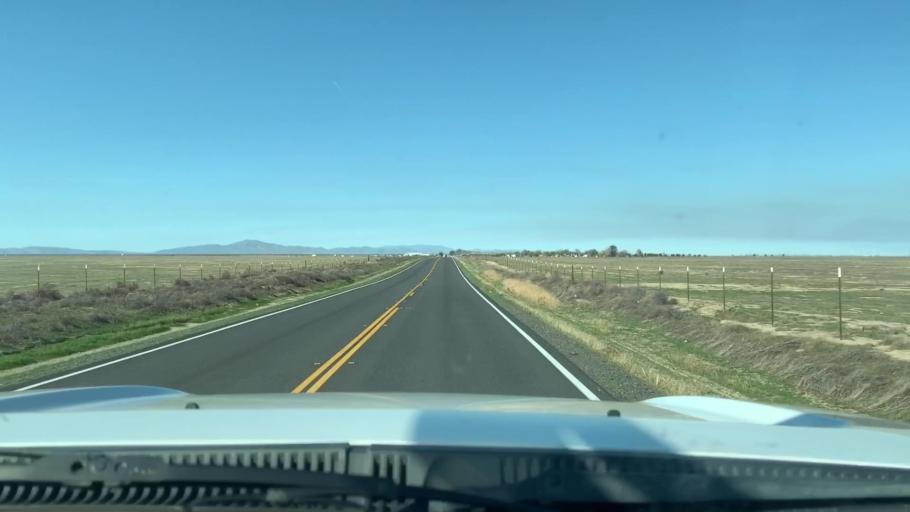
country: US
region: California
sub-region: Kern County
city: Lost Hills
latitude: 35.6000
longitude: -119.8494
